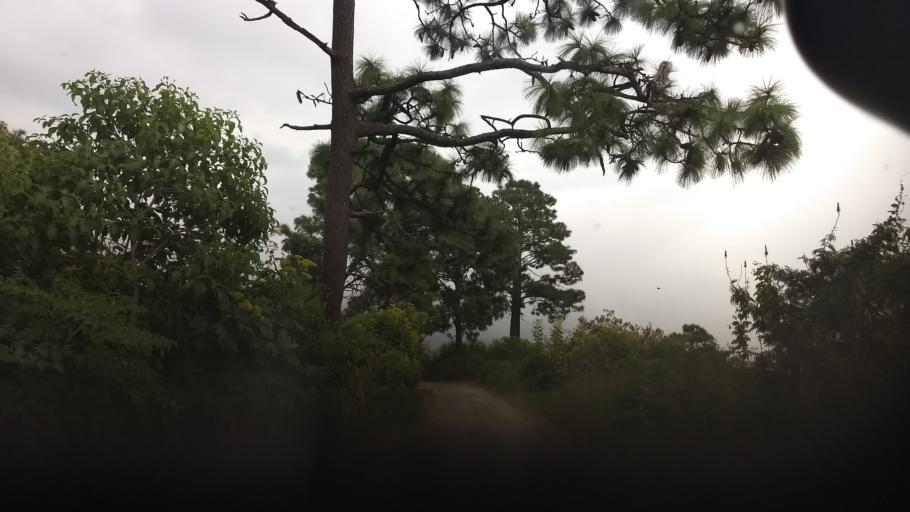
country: MX
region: Colima
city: Cofradia
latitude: 19.4673
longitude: -103.5367
